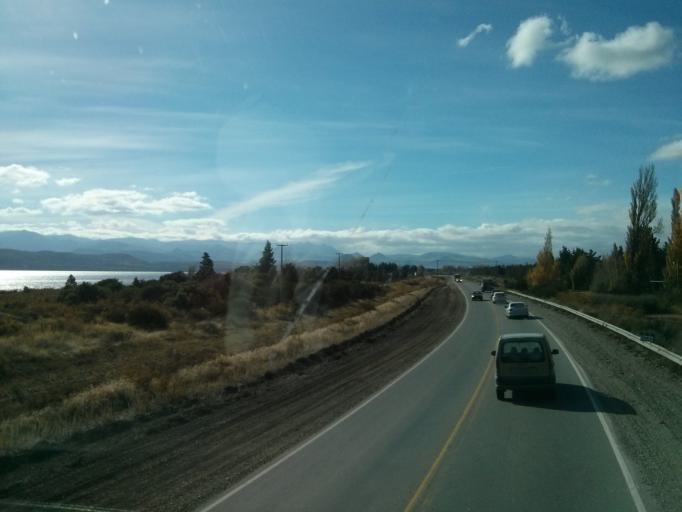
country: AR
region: Rio Negro
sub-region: Departamento de Bariloche
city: San Carlos de Bariloche
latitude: -41.1006
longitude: -71.1870
